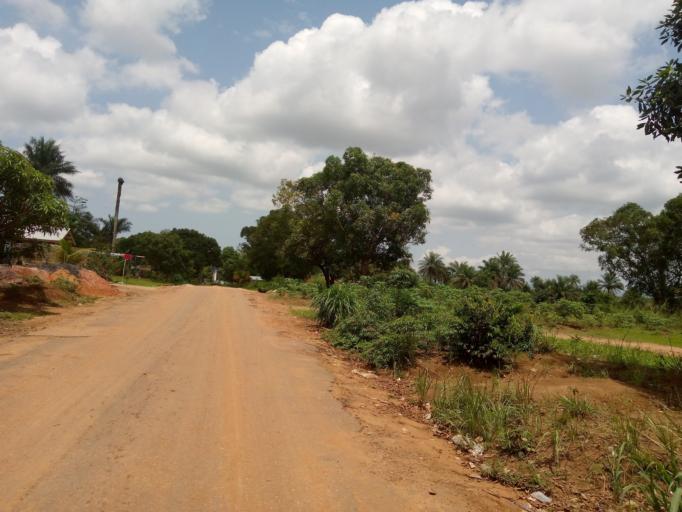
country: SL
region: Western Area
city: Waterloo
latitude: 8.3816
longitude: -12.9584
